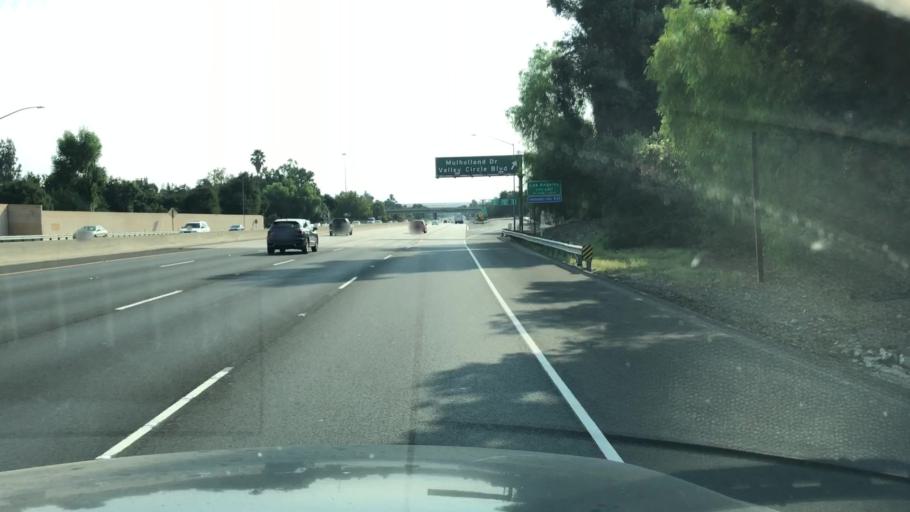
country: US
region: California
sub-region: Los Angeles County
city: Calabasas
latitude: 34.1576
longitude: -118.6420
